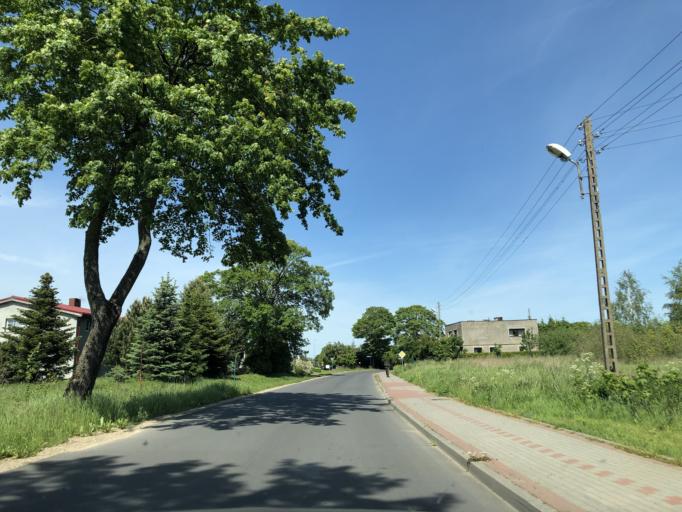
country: PL
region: West Pomeranian Voivodeship
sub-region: Powiat kolobrzeski
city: Dygowo
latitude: 54.1282
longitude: 15.7139
